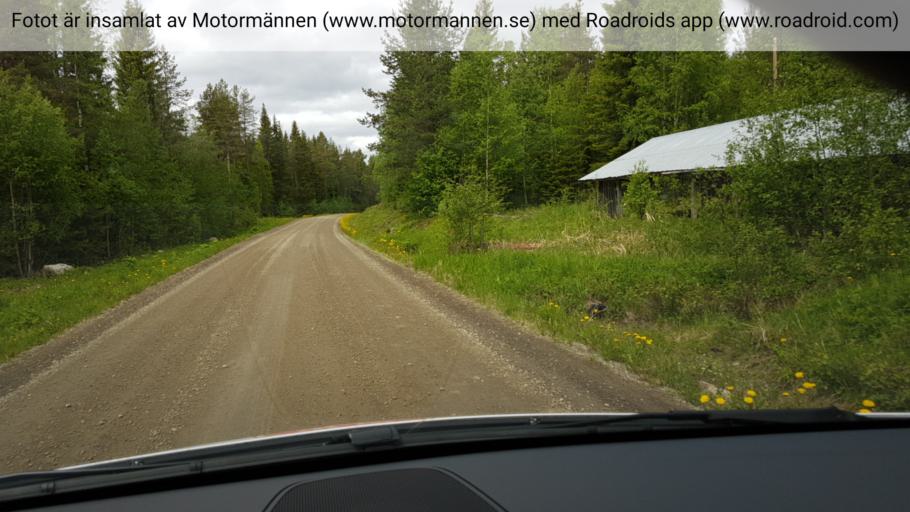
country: SE
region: Jaemtland
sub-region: Braecke Kommun
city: Braecke
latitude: 62.8290
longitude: 15.2103
